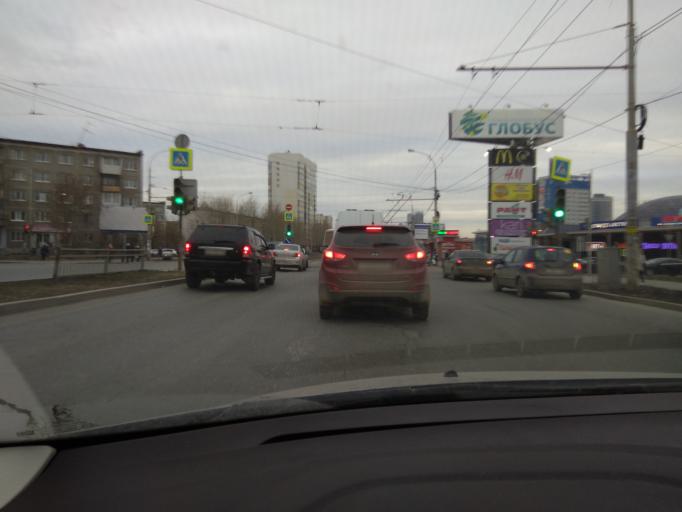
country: RU
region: Sverdlovsk
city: Yekaterinburg
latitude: 56.7869
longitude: 60.6484
